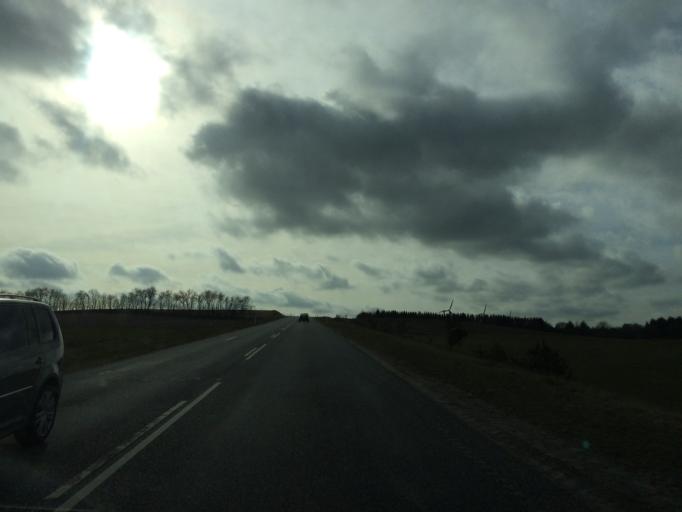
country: DK
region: Central Jutland
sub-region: Randers Kommune
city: Assentoft
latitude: 56.4425
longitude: 10.2198
